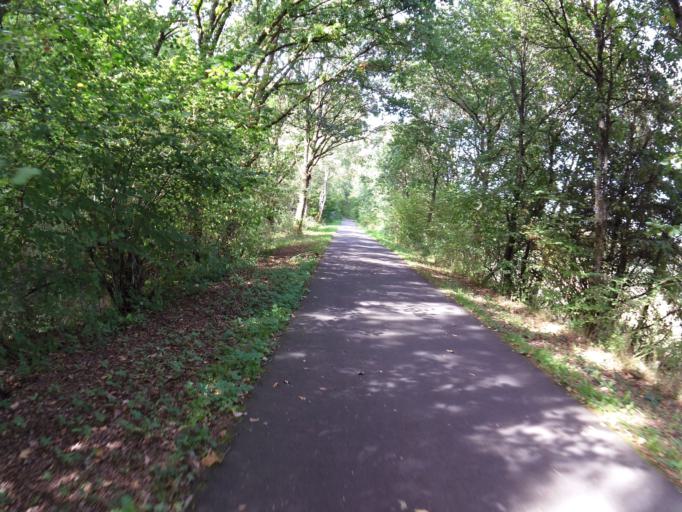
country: DE
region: Rheinland-Pfalz
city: Pronsfeld
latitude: 50.1524
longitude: 6.3354
